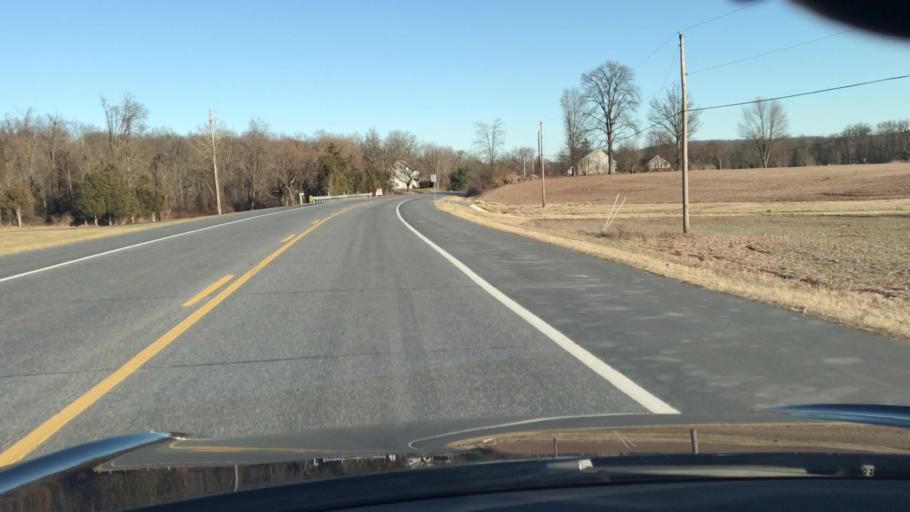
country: US
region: Pennsylvania
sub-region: Cumberland County
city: Lower Allen
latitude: 40.1457
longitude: -76.8782
